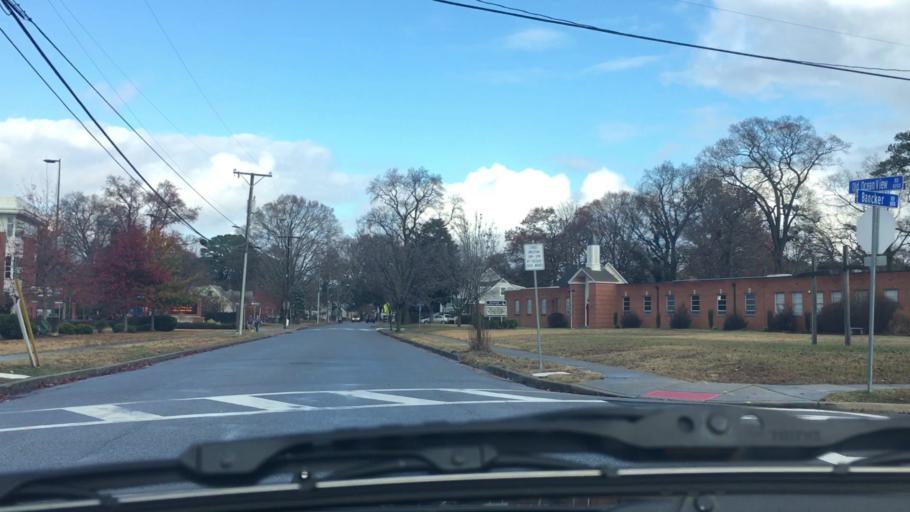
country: US
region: Virginia
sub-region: City of Norfolk
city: Norfolk
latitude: 36.9175
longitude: -76.2508
